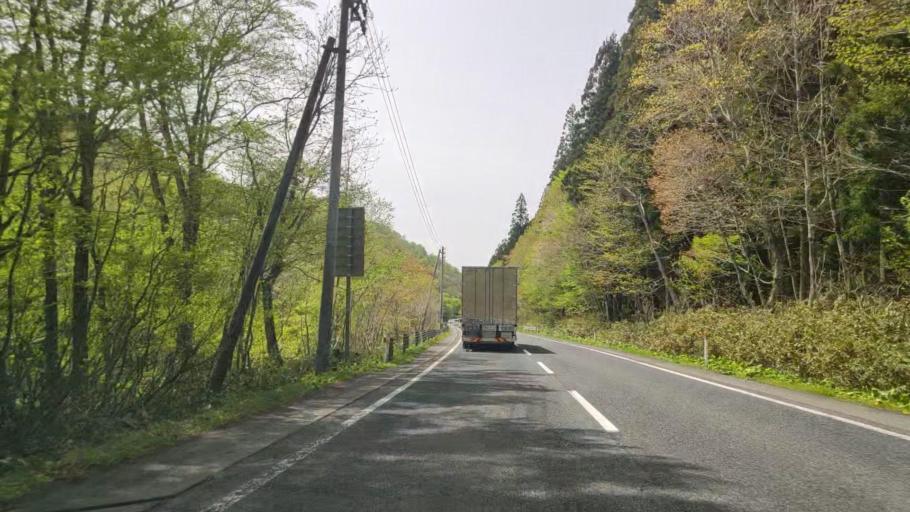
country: JP
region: Aomori
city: Aomori Shi
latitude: 40.7759
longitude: 141.0170
